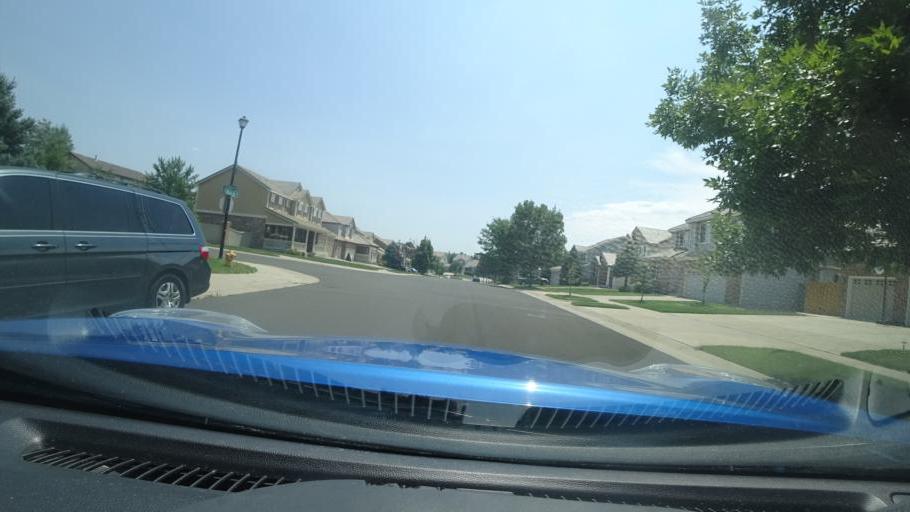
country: US
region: Colorado
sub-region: Adams County
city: Aurora
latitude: 39.6742
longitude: -104.7675
